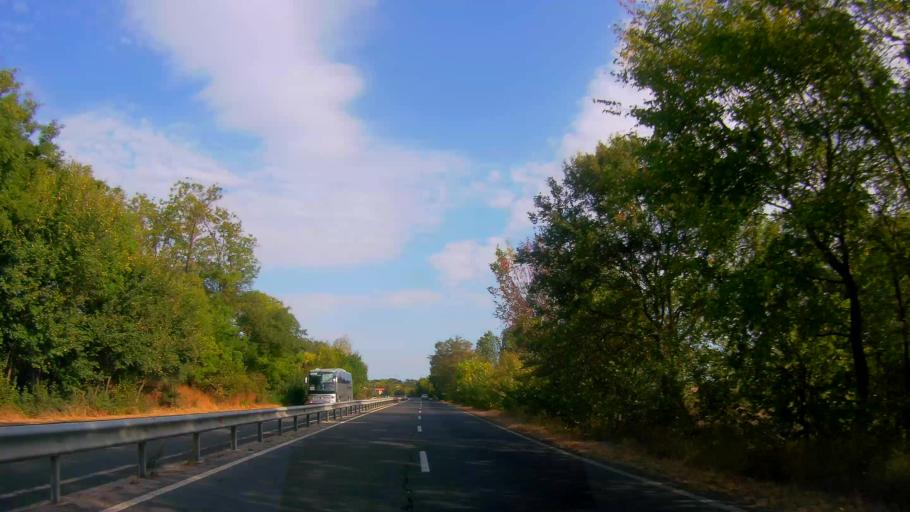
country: BG
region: Burgas
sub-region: Obshtina Sozopol
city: Chernomorets
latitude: 42.4352
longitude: 27.6374
